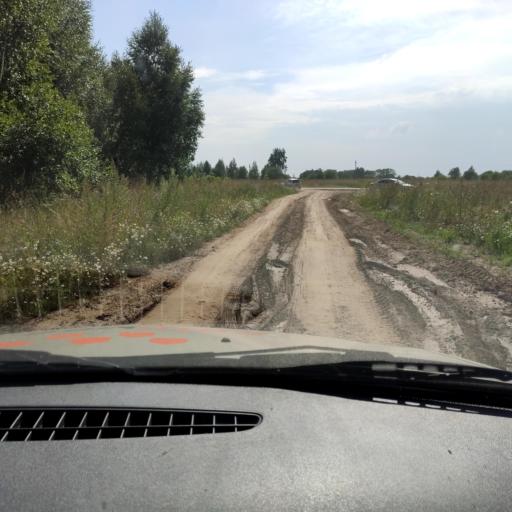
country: RU
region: Bashkortostan
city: Pavlovka
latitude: 55.3968
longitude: 56.4592
